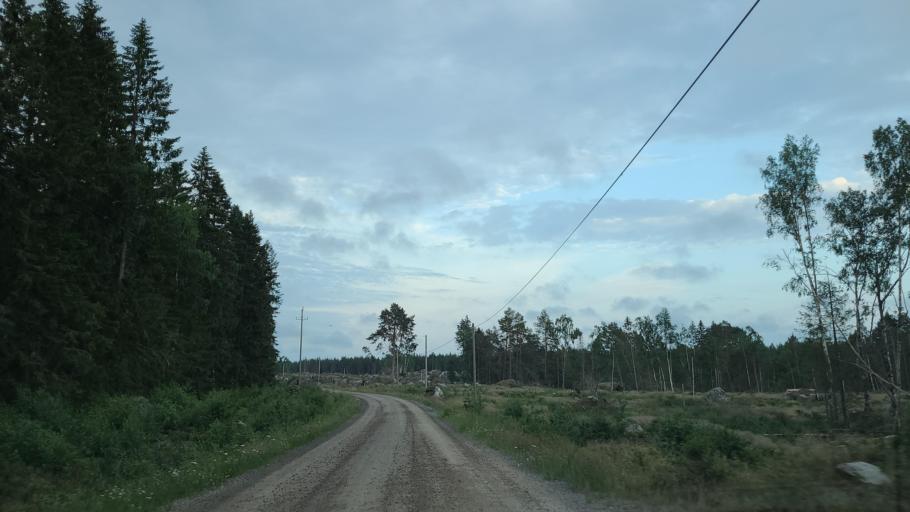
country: FI
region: Ostrobothnia
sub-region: Vaasa
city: Replot
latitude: 63.3198
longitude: 21.1464
